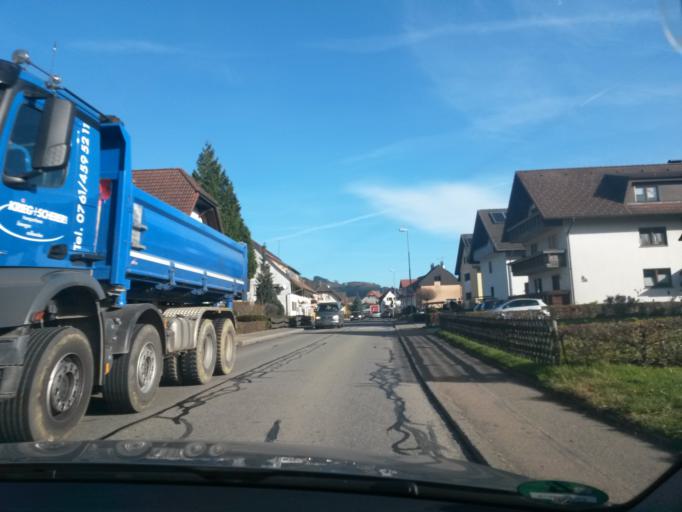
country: DE
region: Baden-Wuerttemberg
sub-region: Freiburg Region
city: Gutach im Breisgau
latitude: 48.1396
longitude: 8.0164
